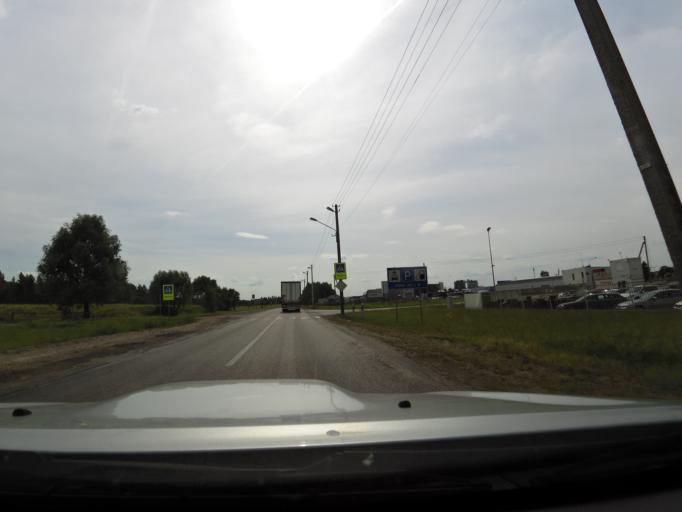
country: LT
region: Marijampoles apskritis
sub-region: Marijampole Municipality
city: Marijampole
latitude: 54.5656
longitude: 23.3849
